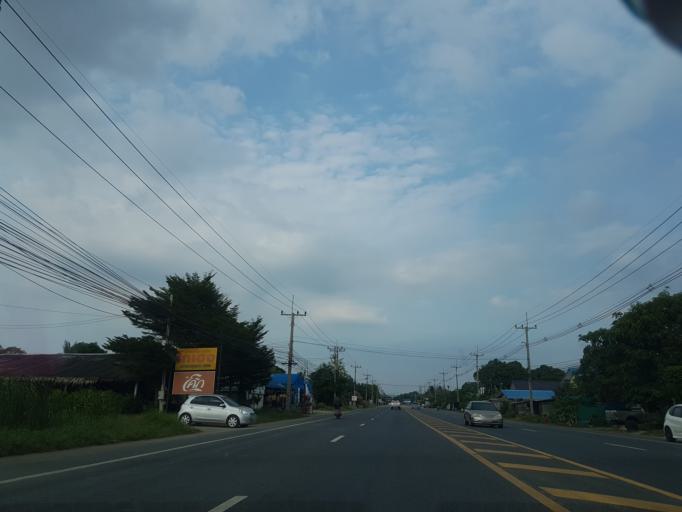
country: TH
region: Sara Buri
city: Phra Phutthabat
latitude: 14.7118
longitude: 100.7837
